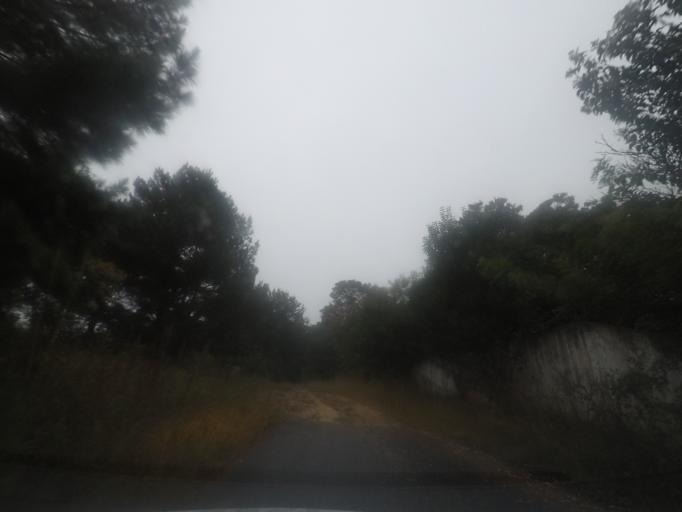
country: BR
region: Parana
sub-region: Curitiba
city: Curitiba
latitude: -25.4142
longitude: -49.2922
